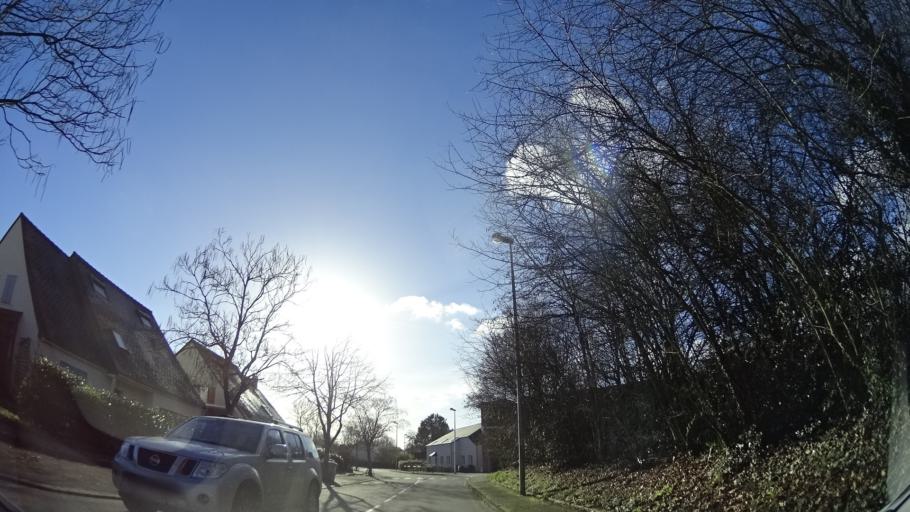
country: FR
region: Brittany
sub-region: Departement d'Ille-et-Vilaine
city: Betton
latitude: 48.1756
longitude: -1.6373
